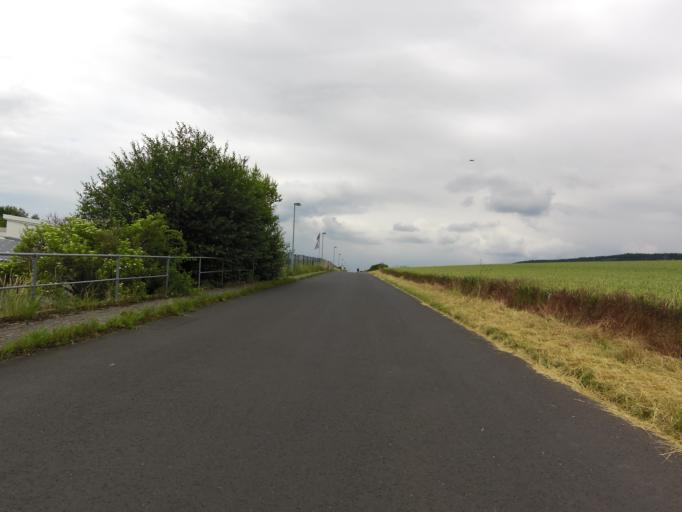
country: DE
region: Thuringia
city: Stadtlengsfeld
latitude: 50.8172
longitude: 10.1234
